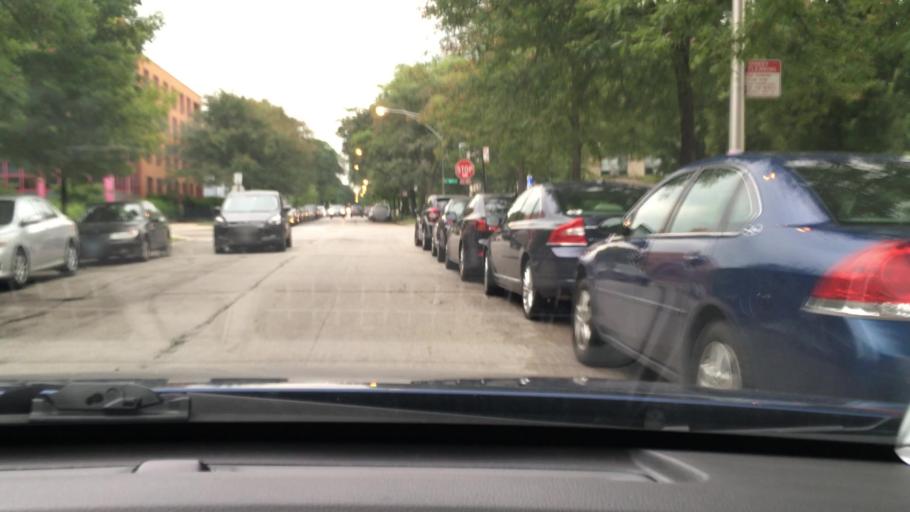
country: US
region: Illinois
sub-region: Cook County
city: Chicago
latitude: 41.7936
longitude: -87.6014
